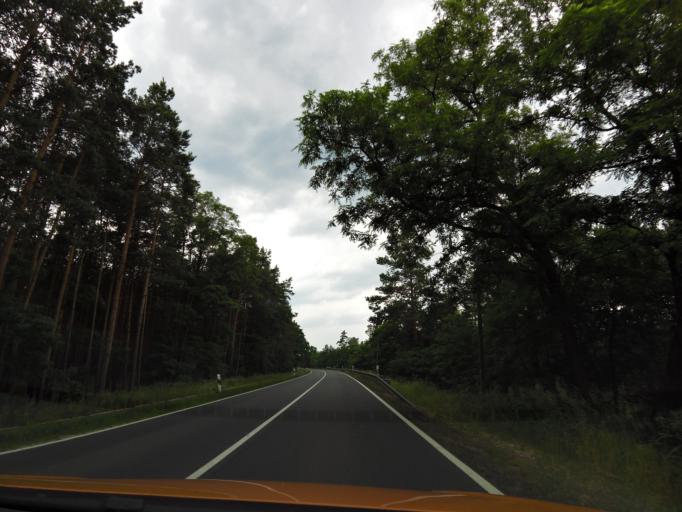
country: DE
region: Brandenburg
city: Baruth
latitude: 52.0284
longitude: 13.5339
